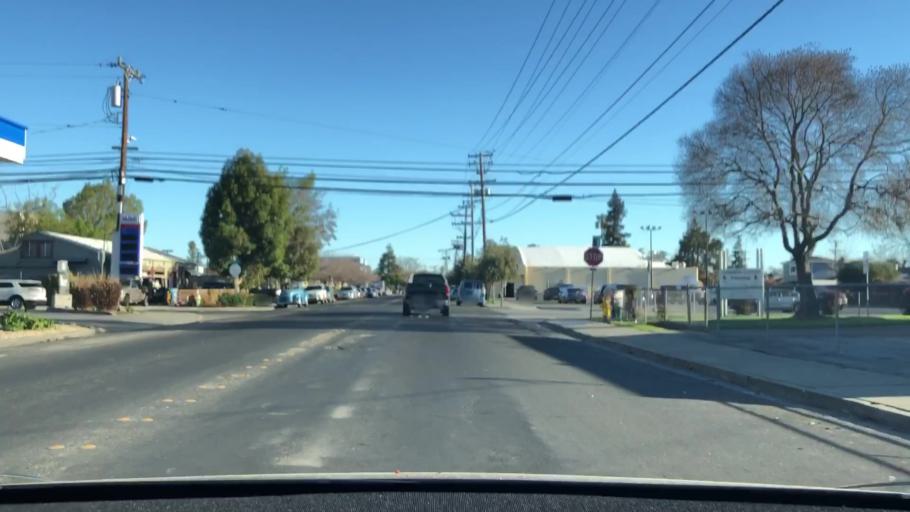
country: US
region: California
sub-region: San Mateo County
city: North Fair Oaks
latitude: 37.4794
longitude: -122.2000
